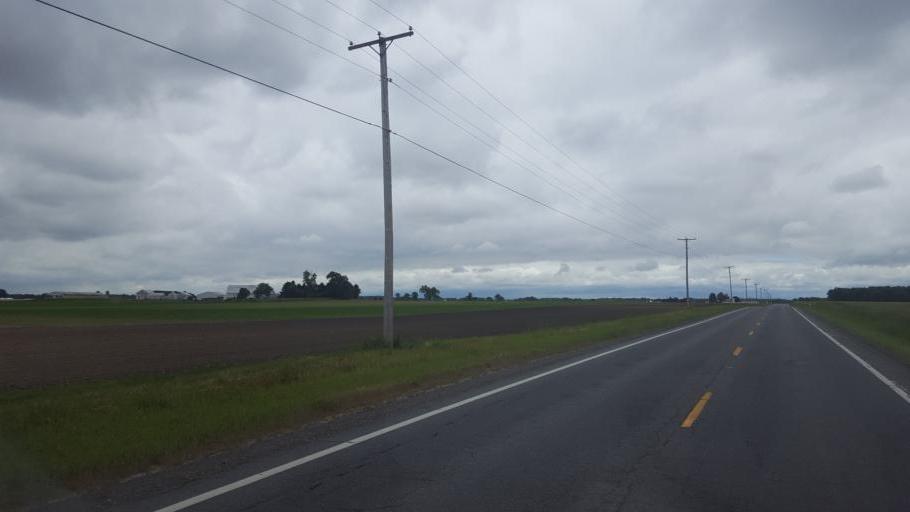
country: US
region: Ohio
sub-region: Crawford County
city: Bucyrus
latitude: 40.7775
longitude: -82.9245
